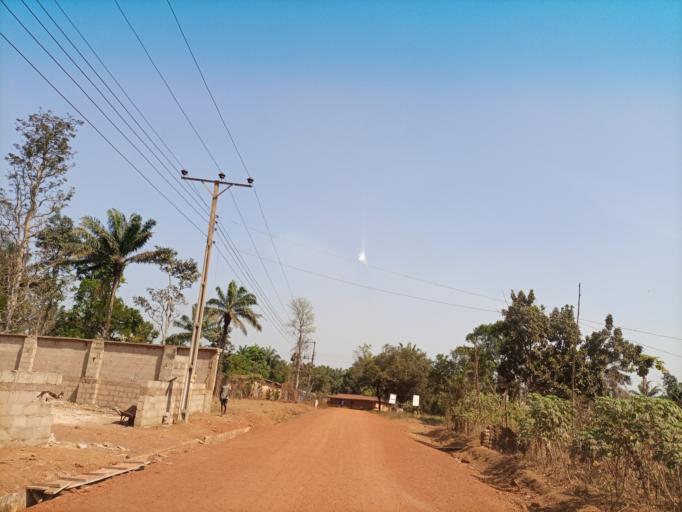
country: NG
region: Enugu
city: Nsukka
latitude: 6.7993
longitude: 7.3518
